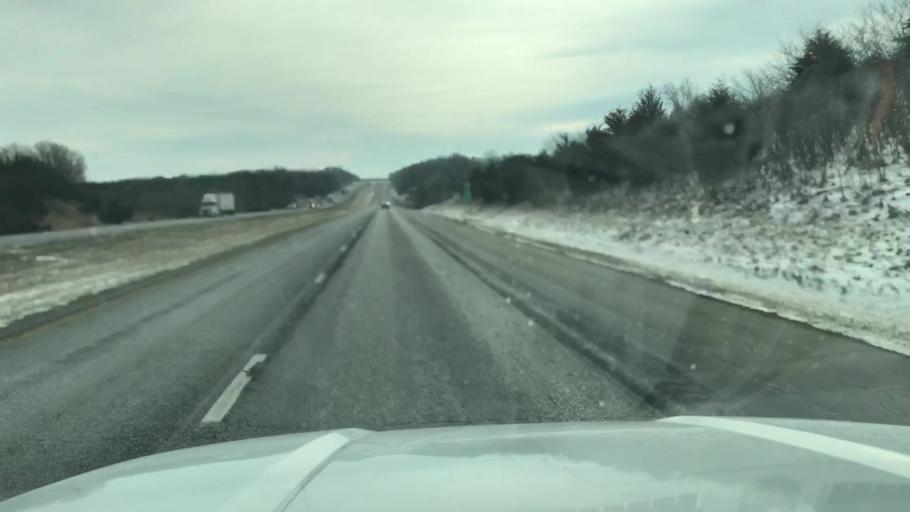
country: US
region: Missouri
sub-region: Holt County
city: Oregon
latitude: 39.9976
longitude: -95.0568
